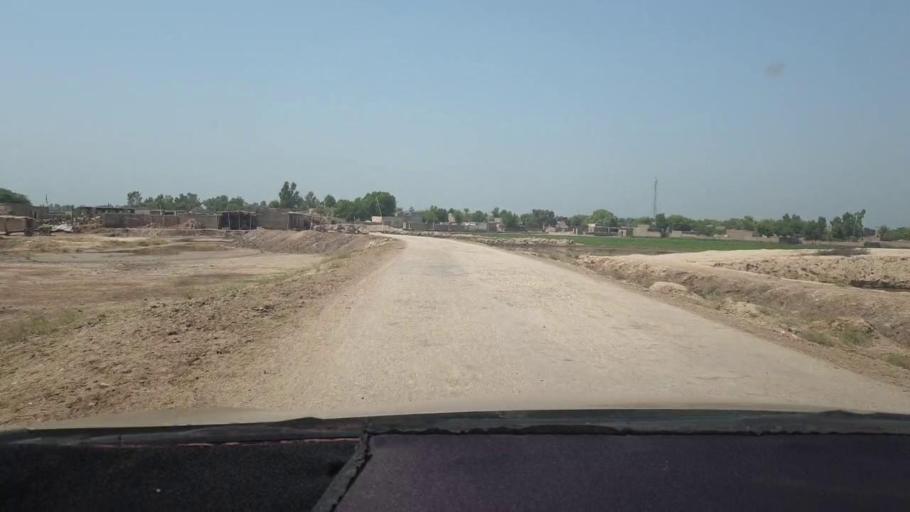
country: PK
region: Sindh
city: Miro Khan
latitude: 27.6676
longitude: 68.0663
